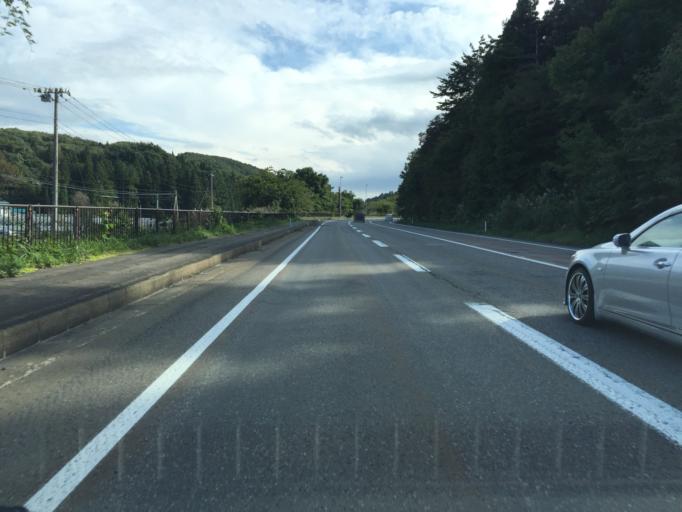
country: JP
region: Fukushima
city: Inawashiro
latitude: 37.5304
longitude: 139.9800
